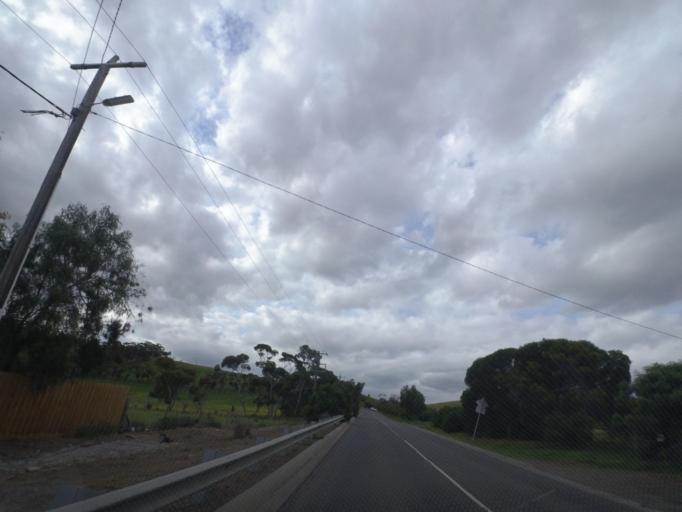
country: AU
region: Victoria
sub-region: Brimbank
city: Keilor
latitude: -37.7021
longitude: 144.8352
